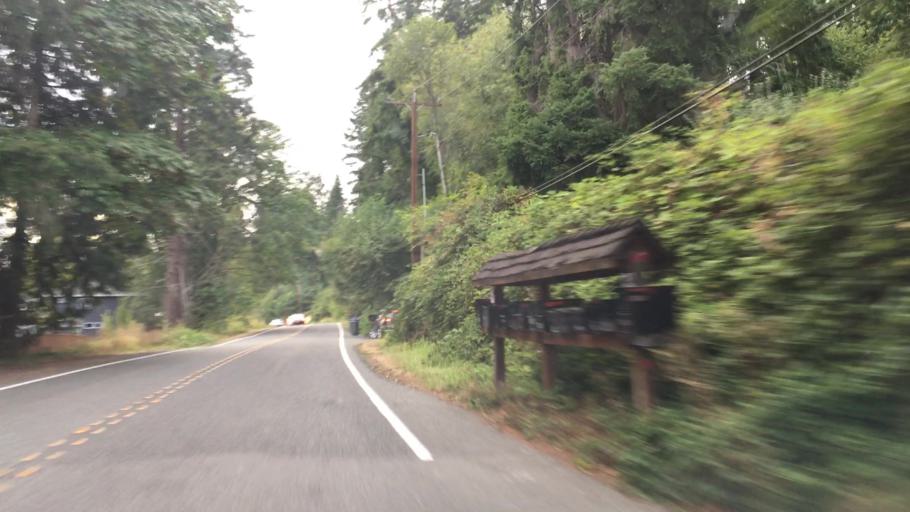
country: US
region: Washington
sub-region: King County
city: West Lake Sammamish
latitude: 47.5796
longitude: -122.1155
